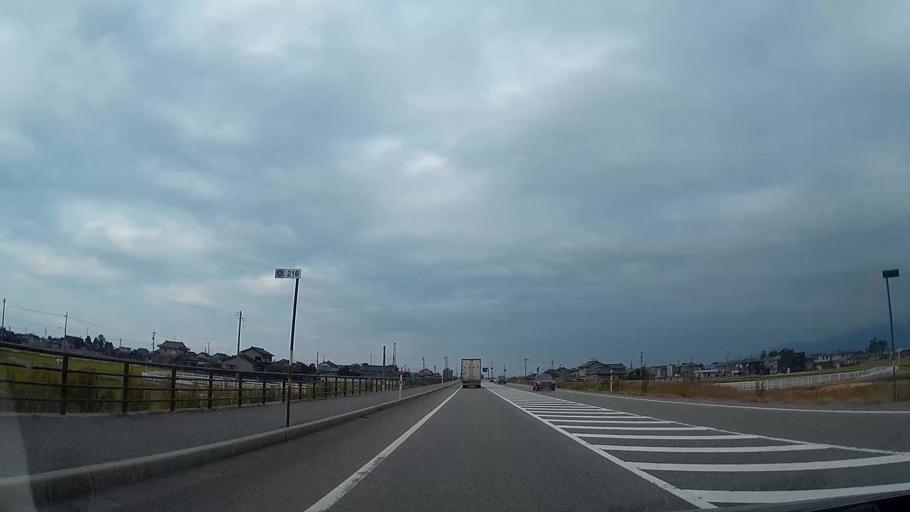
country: JP
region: Toyama
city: Nyuzen
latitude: 36.9189
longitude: 137.4646
